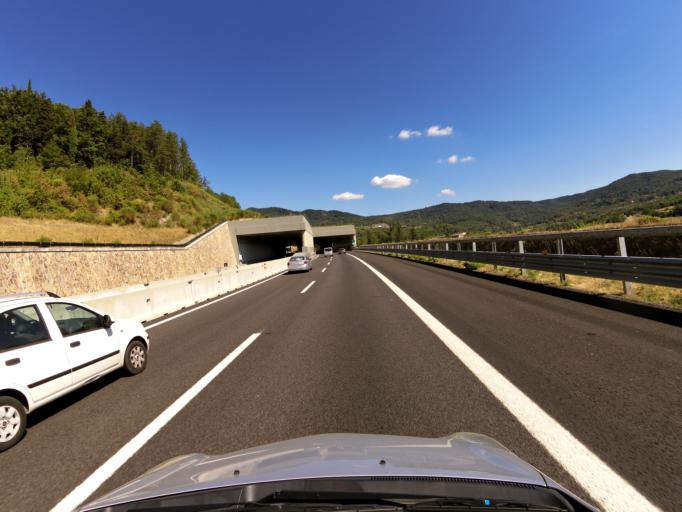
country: IT
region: Tuscany
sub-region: Province of Florence
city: Barberino di Mugello
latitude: 44.0595
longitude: 11.2450
